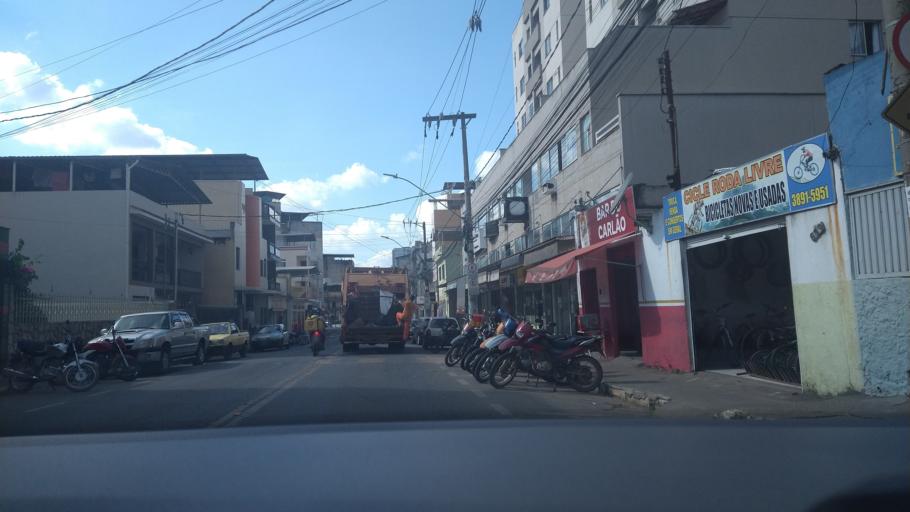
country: BR
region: Minas Gerais
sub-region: Vicosa
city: Vicosa
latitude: -20.7624
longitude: -42.8806
